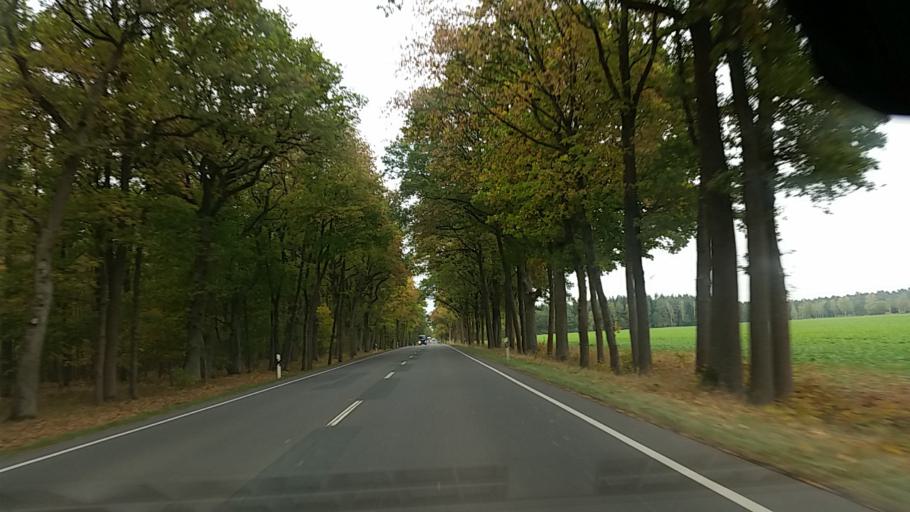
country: DE
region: Lower Saxony
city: Gross Oesingen
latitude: 52.6737
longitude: 10.4692
